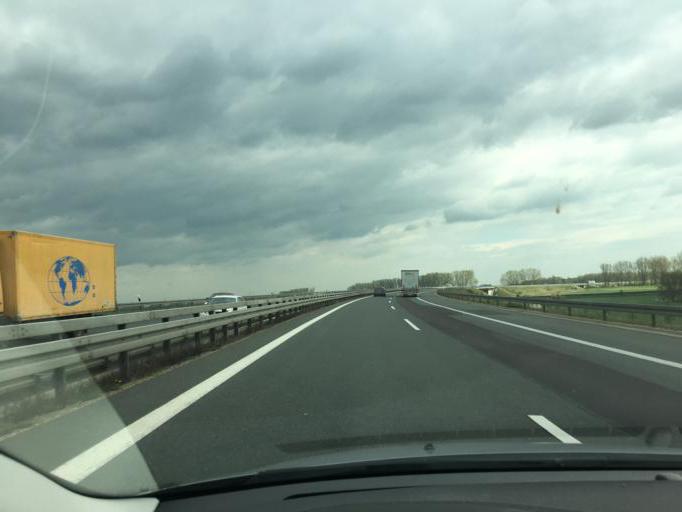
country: DE
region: Saxony-Anhalt
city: Gusten
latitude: 51.8041
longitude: 11.5954
